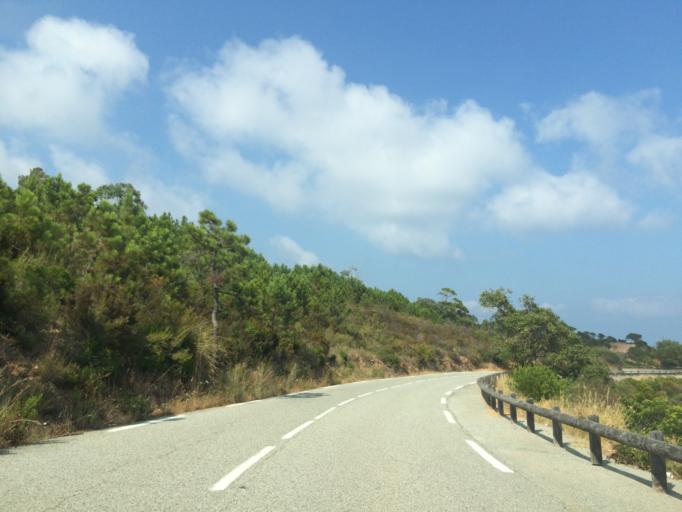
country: FR
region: Provence-Alpes-Cote d'Azur
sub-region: Departement des Alpes-Maritimes
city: Theoule-sur-Mer
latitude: 43.4489
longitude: 6.9143
